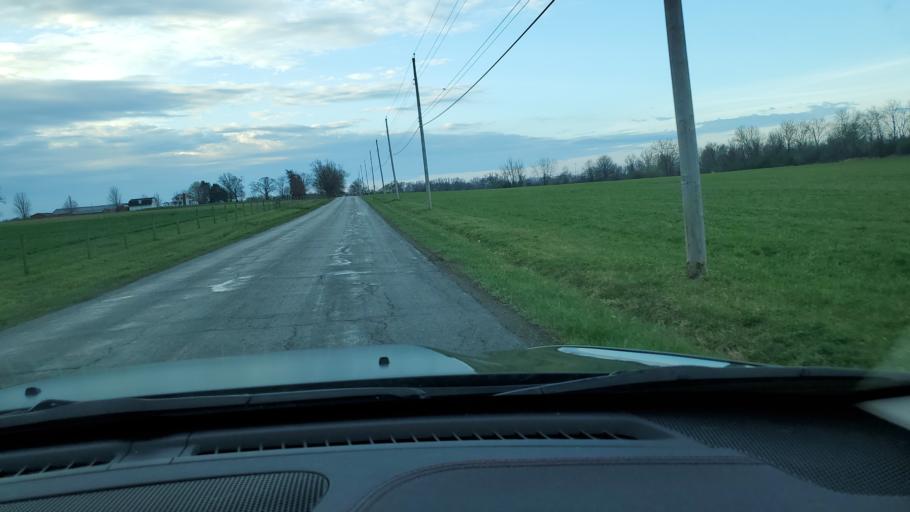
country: US
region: Ohio
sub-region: Trumbull County
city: Mineral Ridge
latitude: 41.1392
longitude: -80.7404
